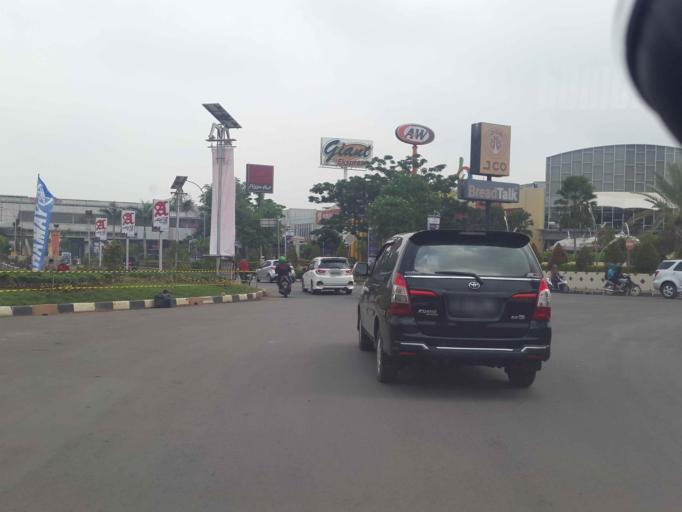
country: ID
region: West Java
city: Cikarang
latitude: -6.3288
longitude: 107.2912
